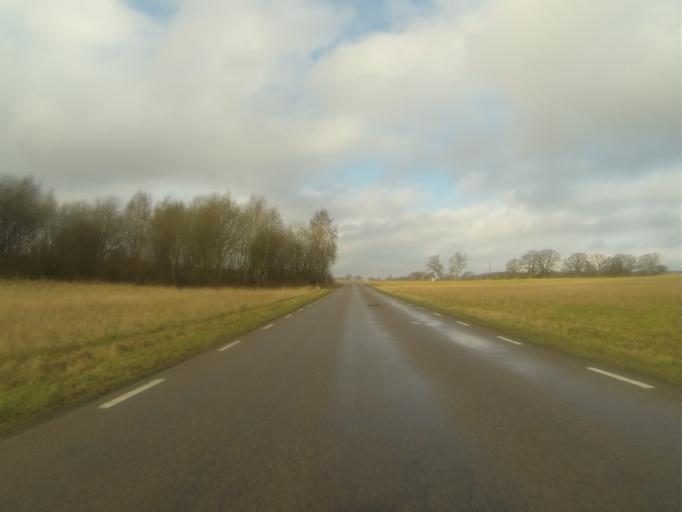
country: SE
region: Skane
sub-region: Svedala Kommun
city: Klagerup
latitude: 55.5656
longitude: 13.3137
